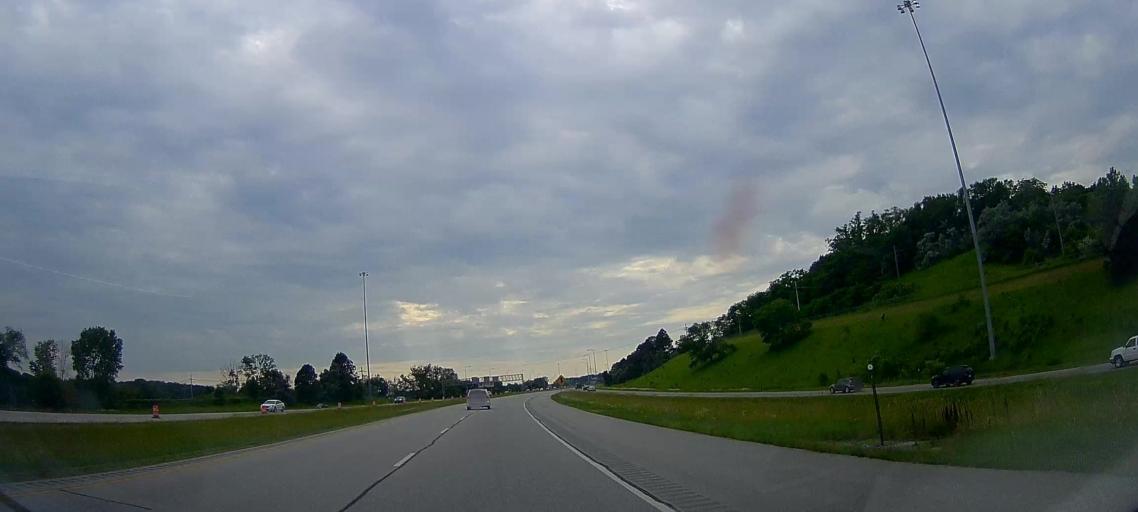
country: US
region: Iowa
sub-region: Pottawattamie County
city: Carter Lake
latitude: 41.3448
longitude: -95.9669
